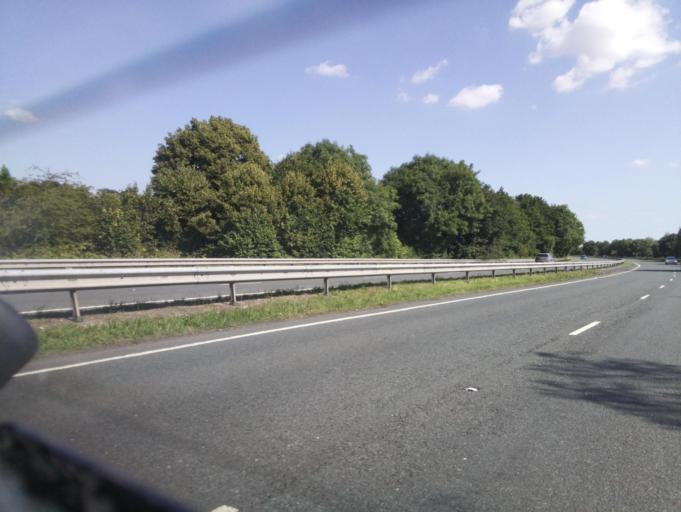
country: GB
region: England
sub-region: Worcestershire
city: Barnt Green
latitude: 52.3177
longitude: -2.0003
